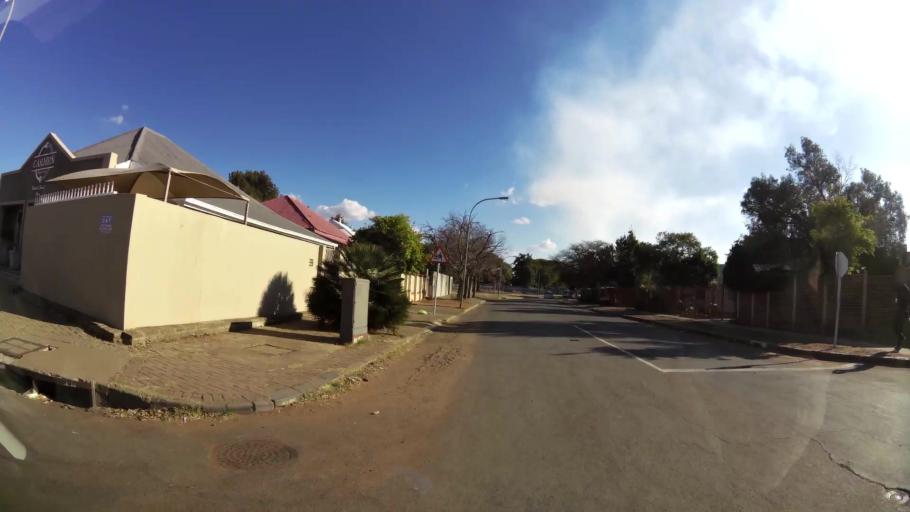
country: ZA
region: Northern Cape
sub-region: Frances Baard District Municipality
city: Kimberley
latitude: -28.7462
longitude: 24.7587
